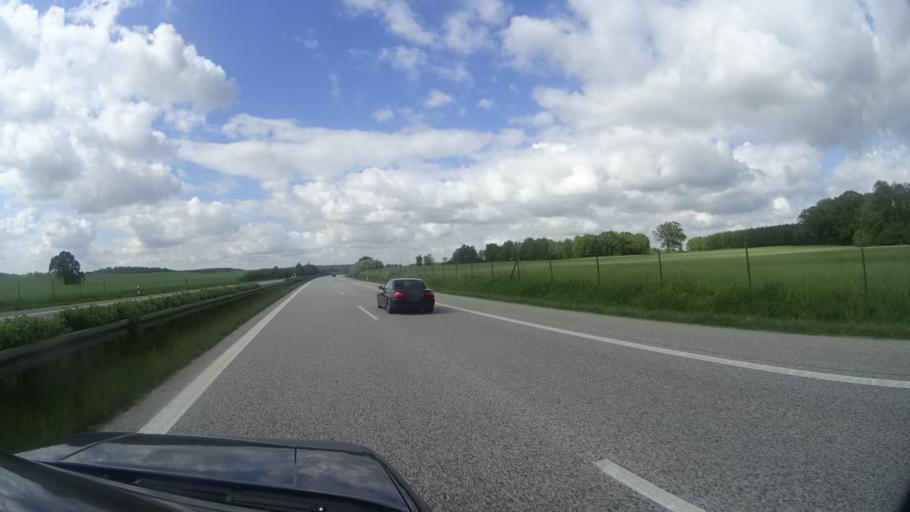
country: DE
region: Mecklenburg-Vorpommern
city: Muhl Rosin
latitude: 53.7990
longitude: 12.2998
